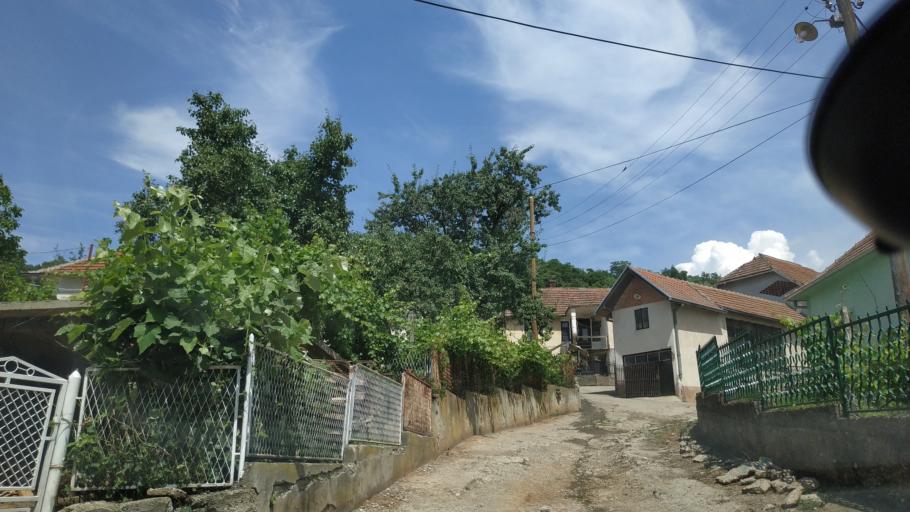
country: RS
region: Central Serbia
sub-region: Nisavski Okrug
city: Aleksinac
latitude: 43.5996
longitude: 21.6986
